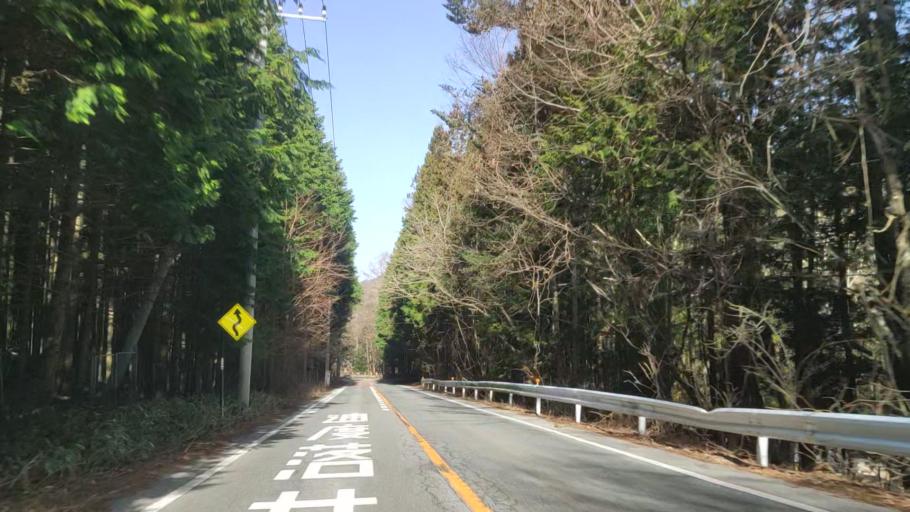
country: JP
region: Yamanashi
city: Fujikawaguchiko
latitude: 35.5513
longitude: 138.6928
